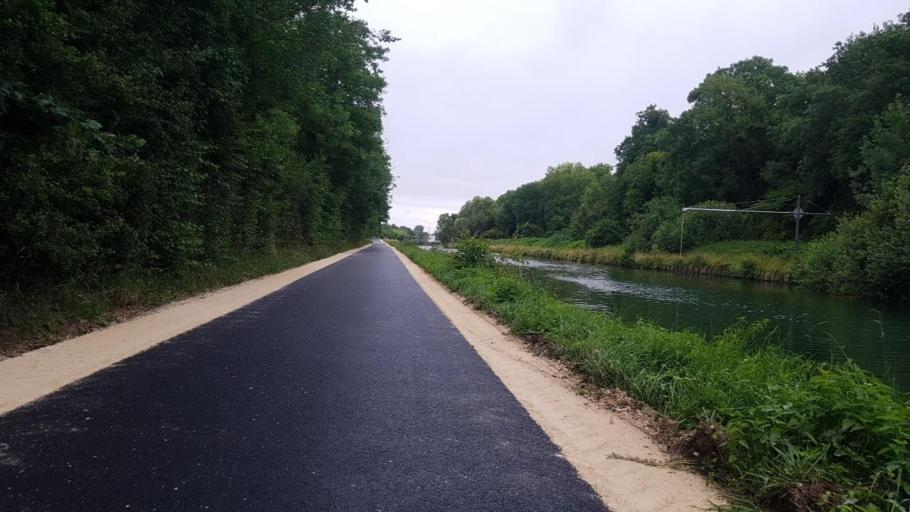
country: FR
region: Champagne-Ardenne
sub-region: Departement de la Marne
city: Vitry-le-Francois
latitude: 48.8058
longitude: 4.5221
